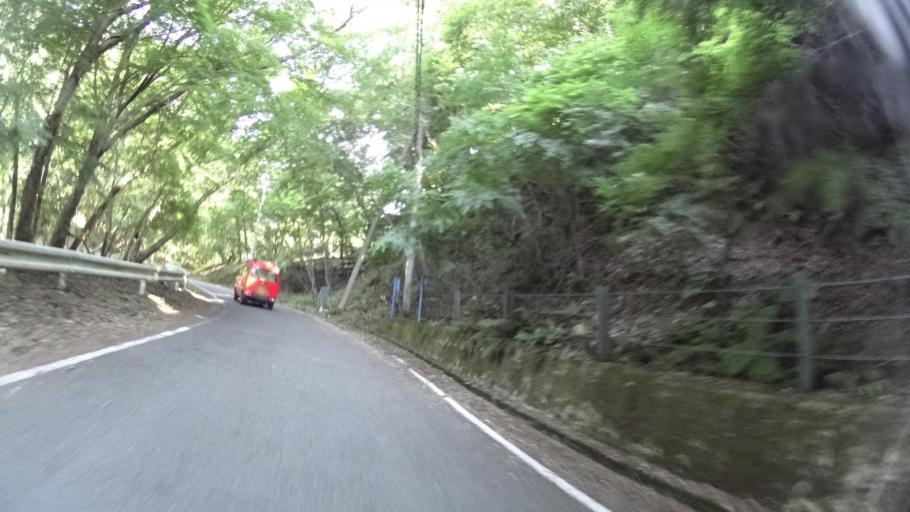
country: JP
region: Kyoto
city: Kameoka
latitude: 34.9924
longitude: 135.5627
